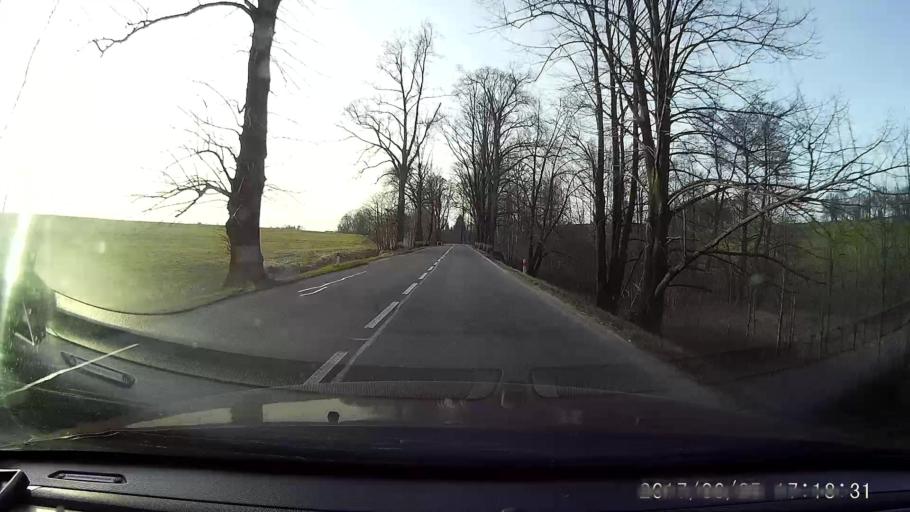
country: PL
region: Silesian Voivodeship
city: Zawidow
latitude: 50.9756
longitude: 15.0816
